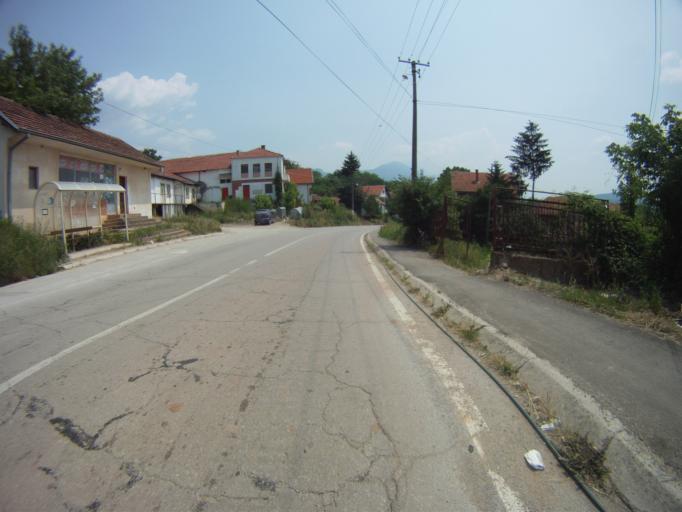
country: RS
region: Central Serbia
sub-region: Nisavski Okrug
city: Gadzin Han
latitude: 43.2399
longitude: 22.0158
